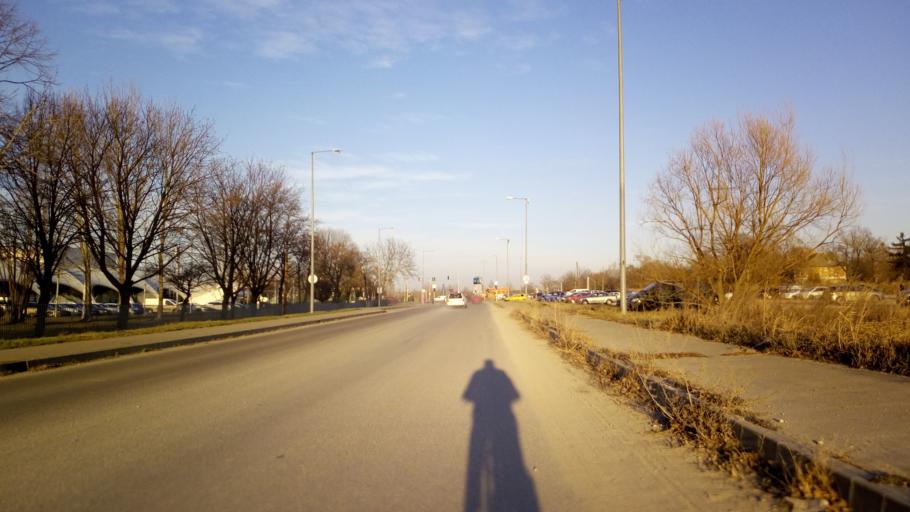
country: HU
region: Baranya
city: Pecs
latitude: 46.0546
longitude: 18.2085
